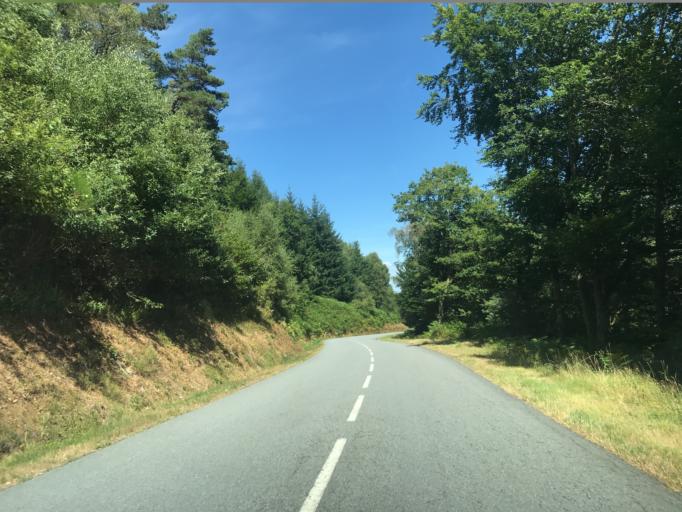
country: FR
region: Limousin
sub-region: Departement de la Creuse
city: Felletin
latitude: 45.7844
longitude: 2.1466
